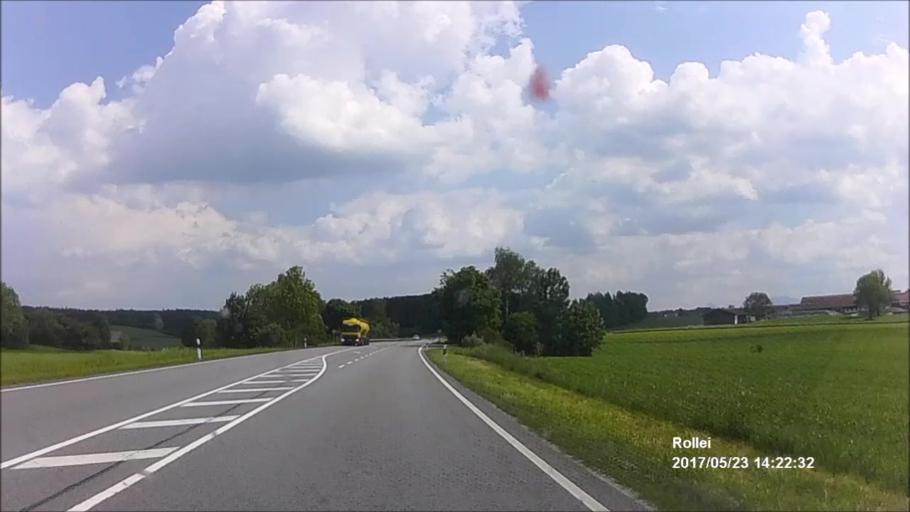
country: DE
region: Bavaria
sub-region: Upper Bavaria
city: Babensham
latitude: 48.0543
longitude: 12.2784
